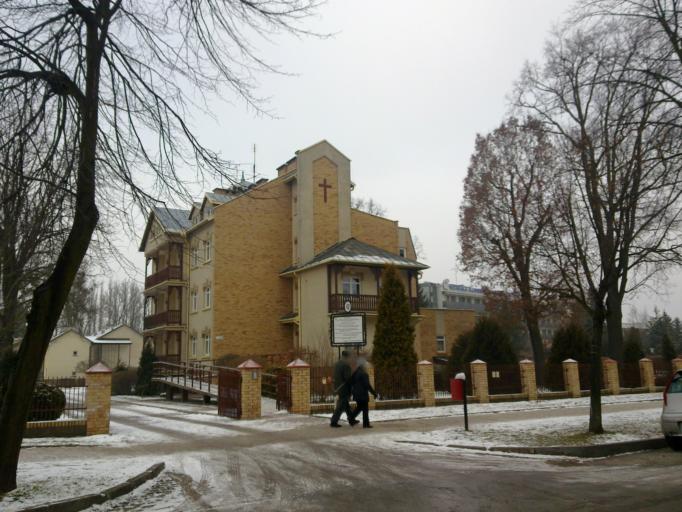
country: PL
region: Kujawsko-Pomorskie
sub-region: Powiat aleksandrowski
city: Ciechocinek
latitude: 52.8844
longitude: 18.7932
